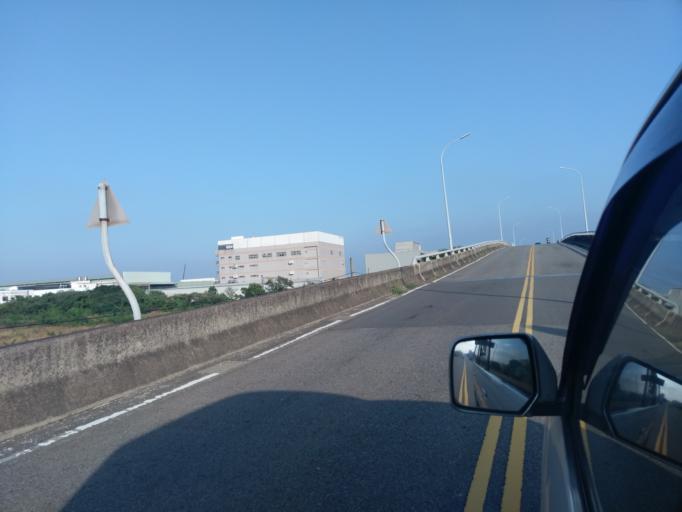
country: TW
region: Taiwan
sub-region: Miaoli
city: Miaoli
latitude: 24.6762
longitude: 120.8784
